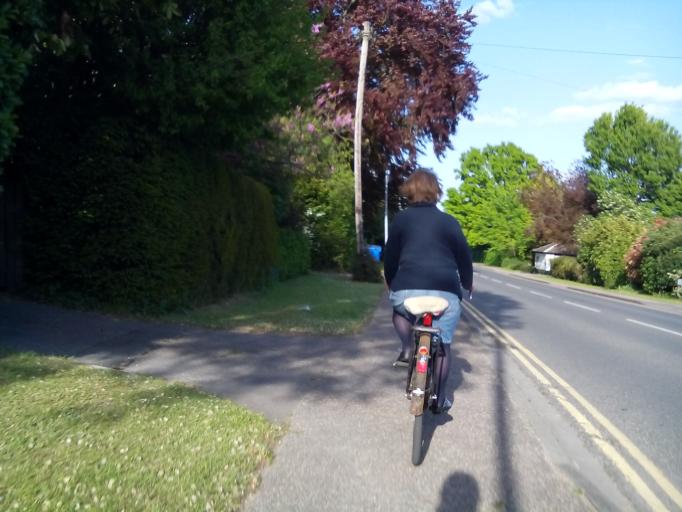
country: GB
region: England
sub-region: Cambridgeshire
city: Cambridge
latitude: 52.1789
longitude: 0.1445
